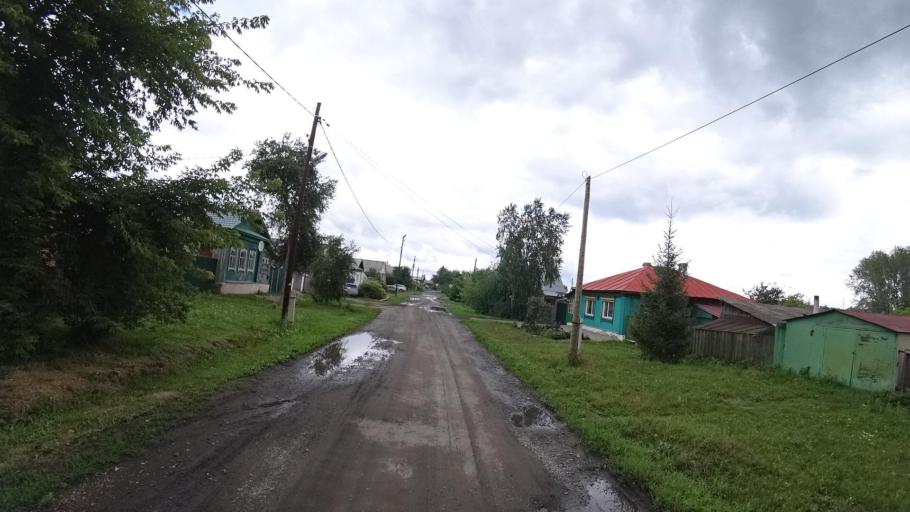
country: RU
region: Sverdlovsk
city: Kamyshlov
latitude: 56.8510
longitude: 62.6884
